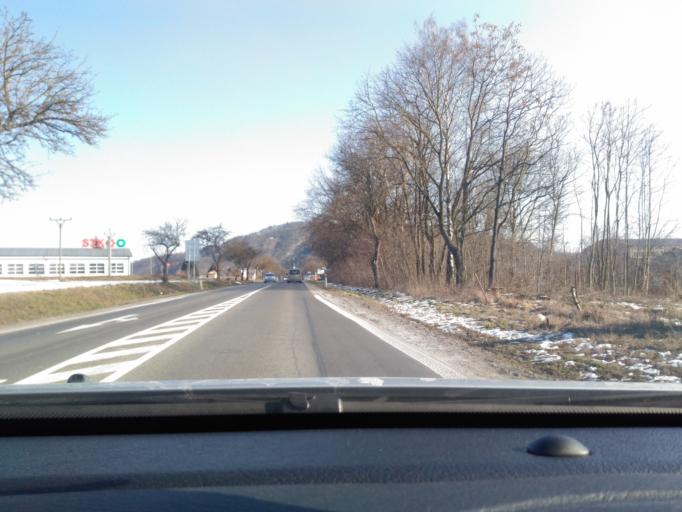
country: CZ
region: South Moravian
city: Kurim
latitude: 49.3002
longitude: 16.5179
